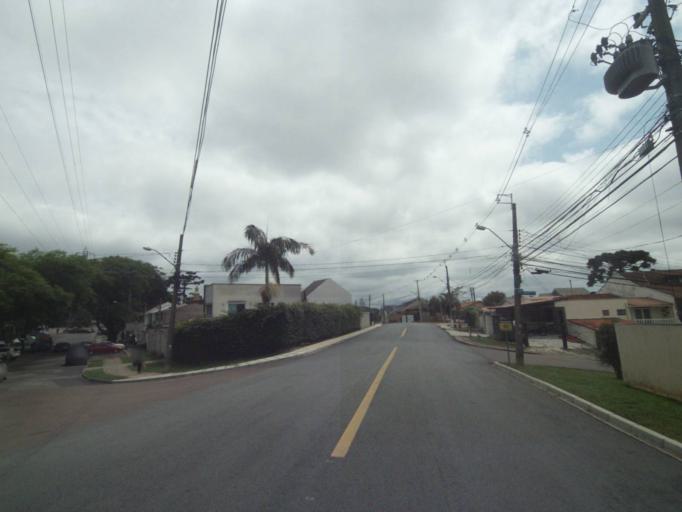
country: BR
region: Parana
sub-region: Curitiba
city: Curitiba
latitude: -25.3869
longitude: -49.2799
